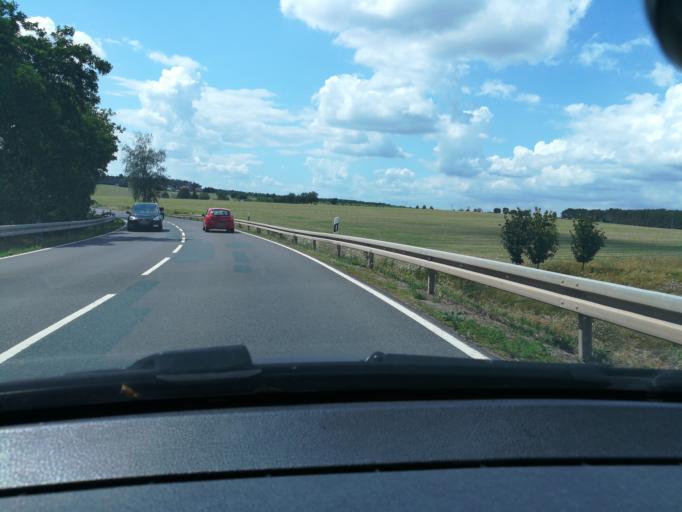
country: DE
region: Saxony-Anhalt
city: Zielitz
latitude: 52.2858
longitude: 11.6722
